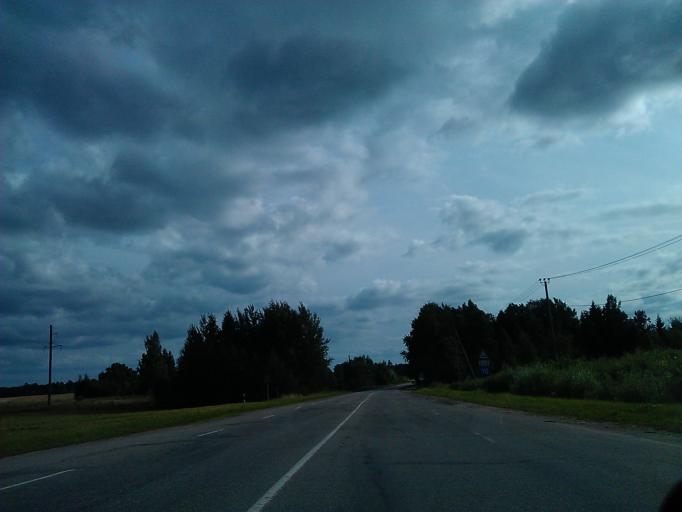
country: LV
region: Cesu Rajons
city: Cesis
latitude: 57.2931
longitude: 25.3040
